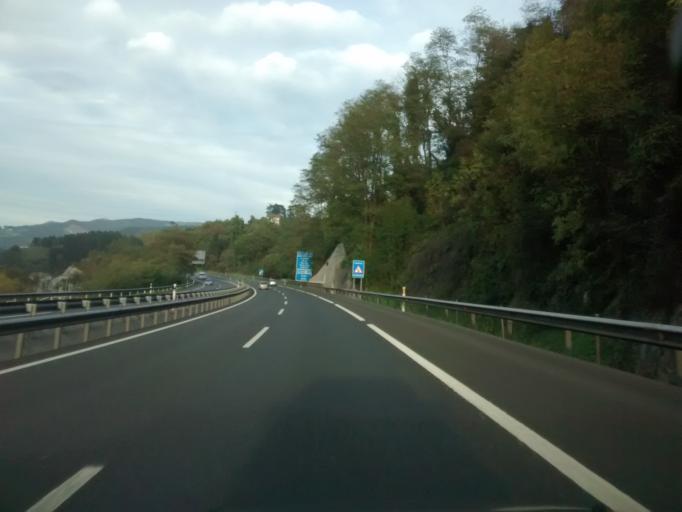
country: ES
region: Basque Country
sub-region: Provincia de Guipuzcoa
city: Elgoibar
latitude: 43.2037
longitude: -2.4242
